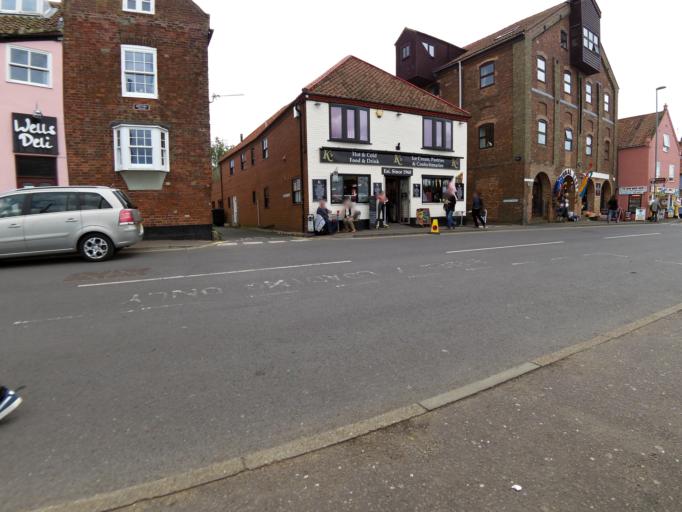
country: GB
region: England
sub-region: Norfolk
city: Wells-next-the-Sea
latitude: 52.9574
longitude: 0.8513
